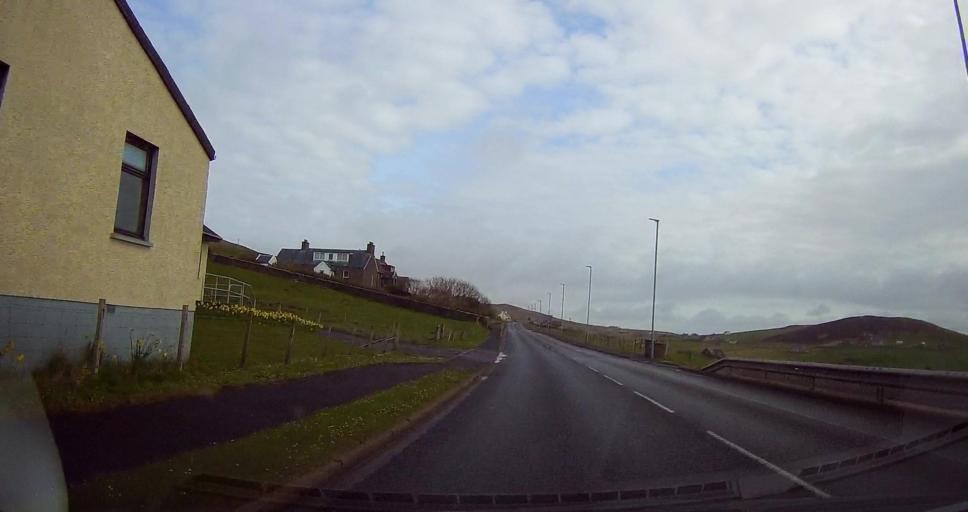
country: GB
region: Scotland
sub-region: Shetland Islands
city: Sandwick
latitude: 60.0457
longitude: -1.2274
